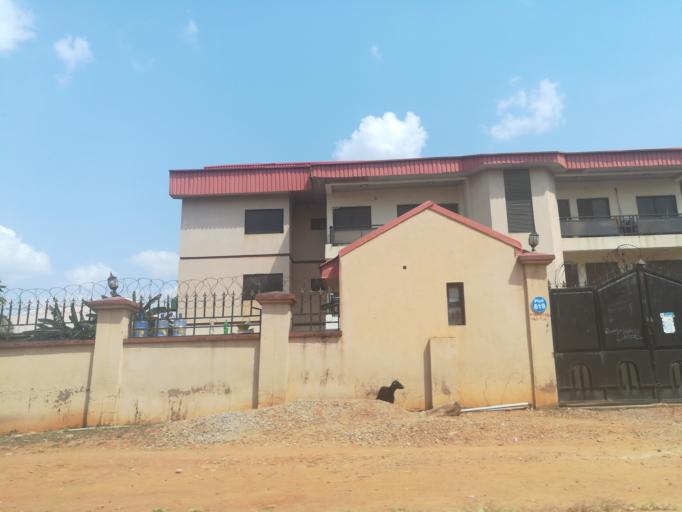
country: NG
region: Abuja Federal Capital Territory
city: Abuja
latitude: 9.0493
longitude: 7.4449
